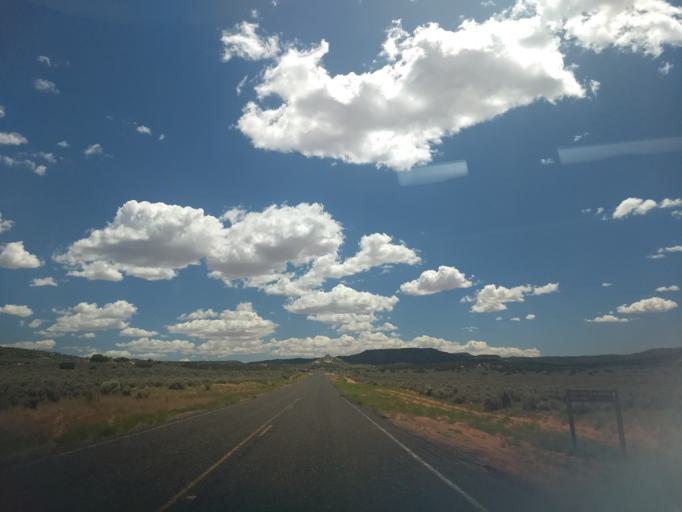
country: US
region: Utah
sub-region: Kane County
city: Kanab
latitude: 37.1613
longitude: -112.6667
